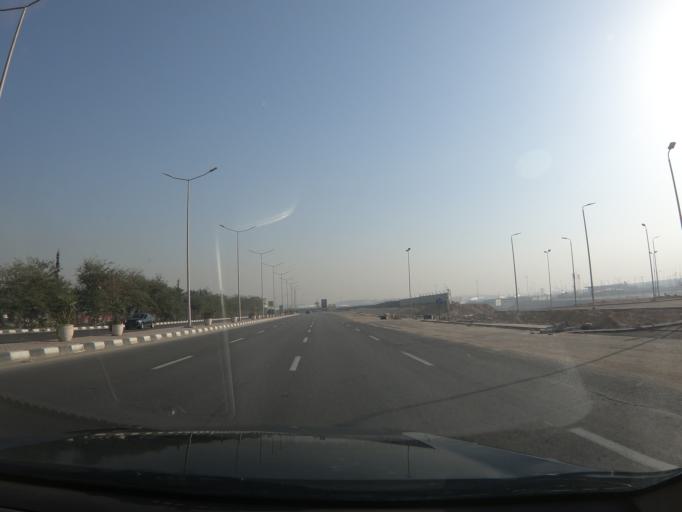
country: EG
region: Muhafazat al Qalyubiyah
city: Al Khankah
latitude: 30.1004
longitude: 31.3865
